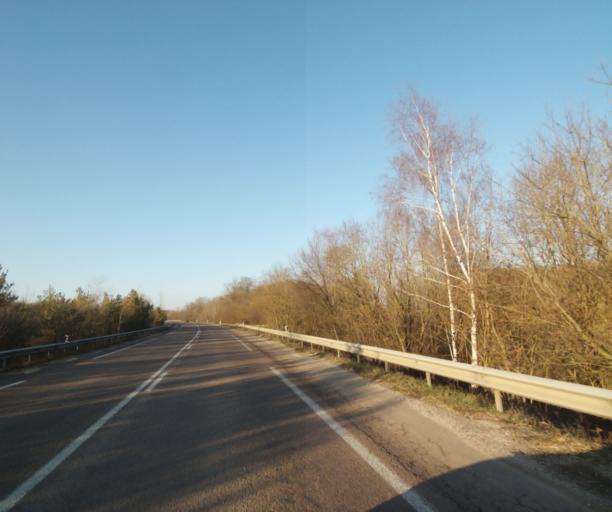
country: FR
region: Champagne-Ardenne
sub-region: Departement de la Haute-Marne
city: Chevillon
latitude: 48.4970
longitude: 5.1095
